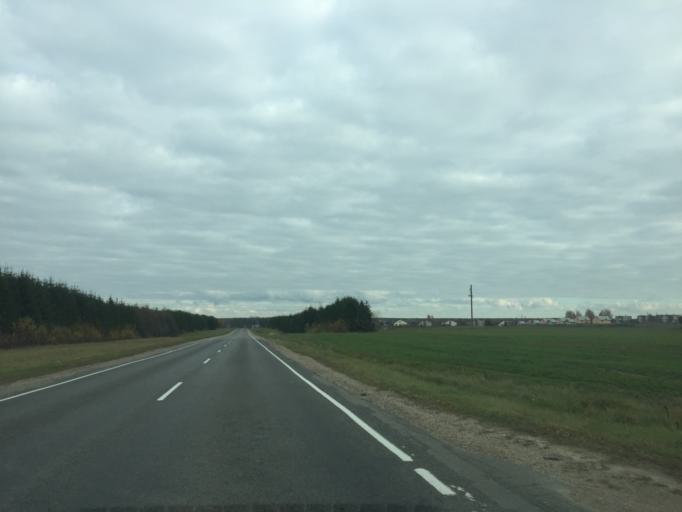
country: BY
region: Minsk
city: Svir
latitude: 54.8075
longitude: 26.1401
